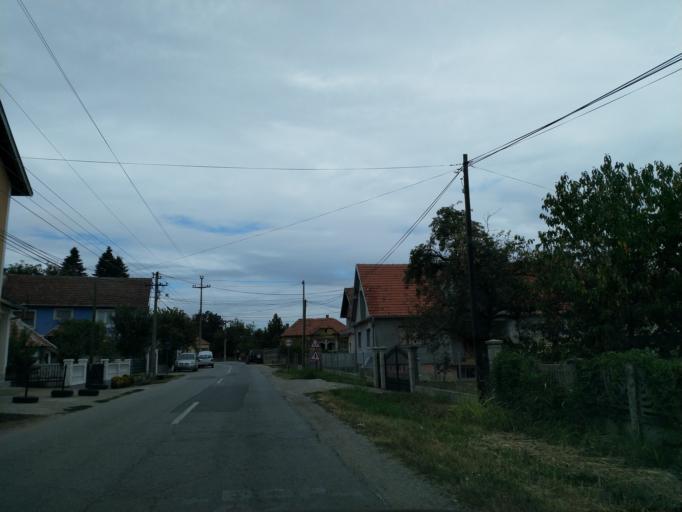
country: RS
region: Central Serbia
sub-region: Pomoravski Okrug
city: Paracin
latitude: 43.8362
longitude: 21.3219
